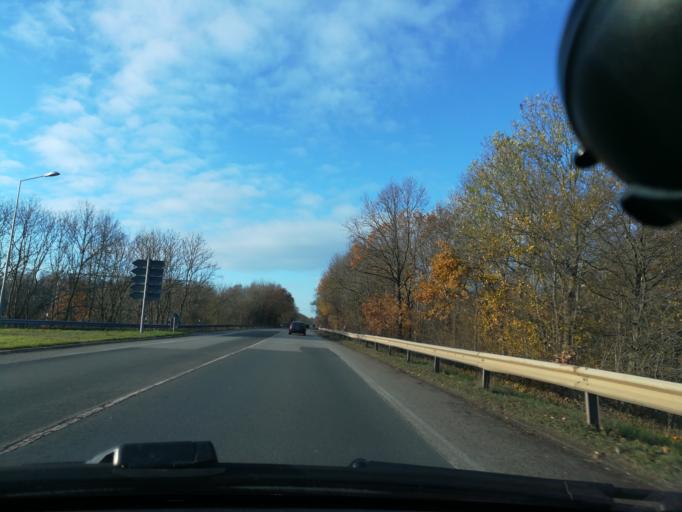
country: DE
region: North Rhine-Westphalia
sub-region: Regierungsbezirk Detmold
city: Petershagen
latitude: 52.3770
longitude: 8.9950
